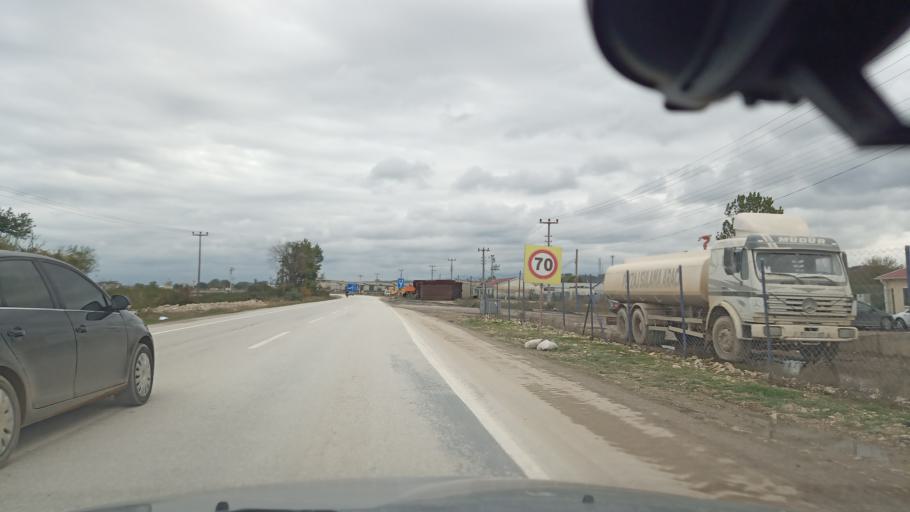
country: TR
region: Sakarya
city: Karasu
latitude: 41.1143
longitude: 30.6556
